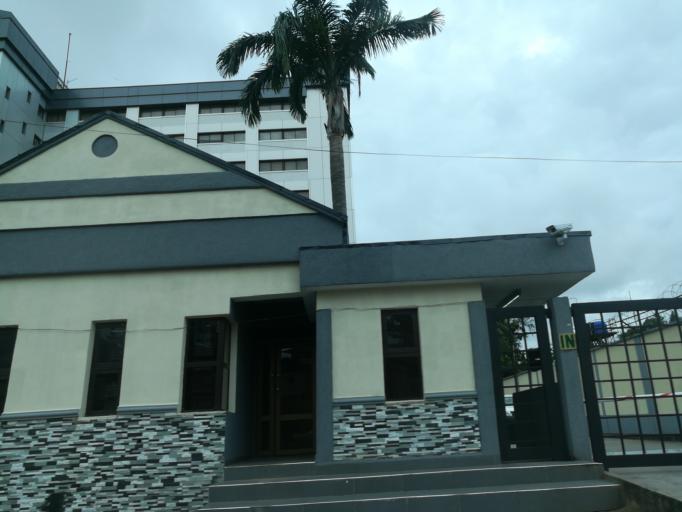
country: NG
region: Lagos
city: Lagos
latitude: 6.4362
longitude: 3.4131
